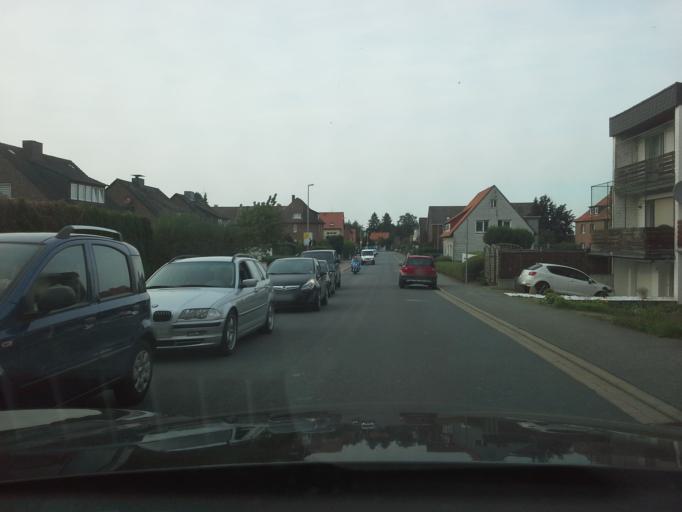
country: DE
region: Lower Saxony
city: Egestorf
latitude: 52.2792
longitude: 9.5157
